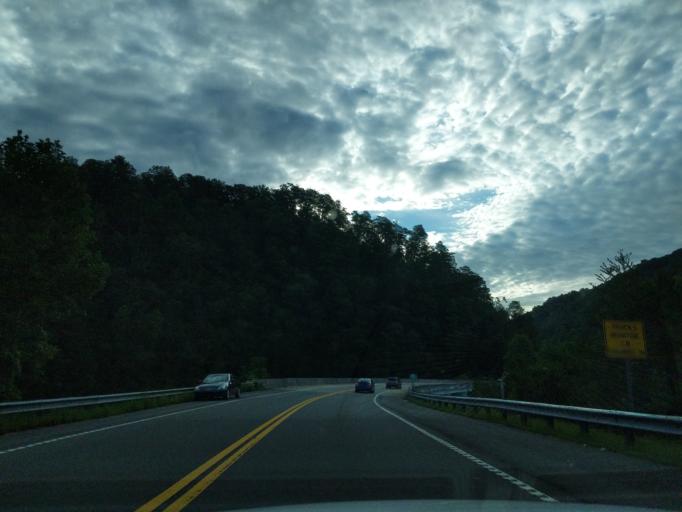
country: US
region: Tennessee
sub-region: Polk County
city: Benton
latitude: 35.1118
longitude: -84.5718
